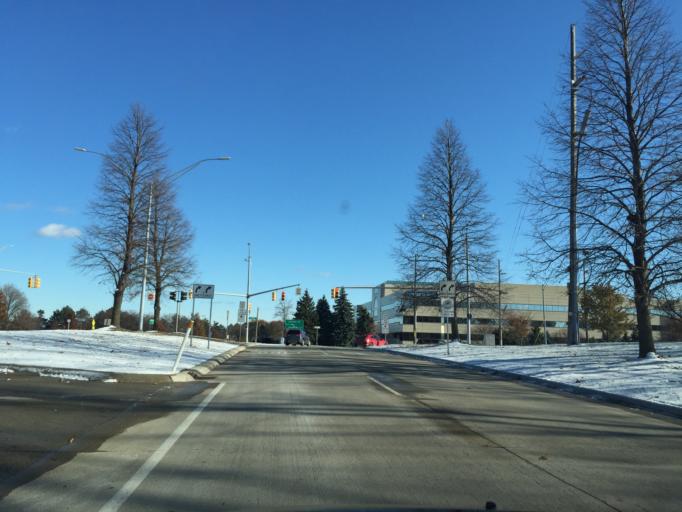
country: US
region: Michigan
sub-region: Oakland County
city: Auburn Hills
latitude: 42.6497
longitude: -83.2213
